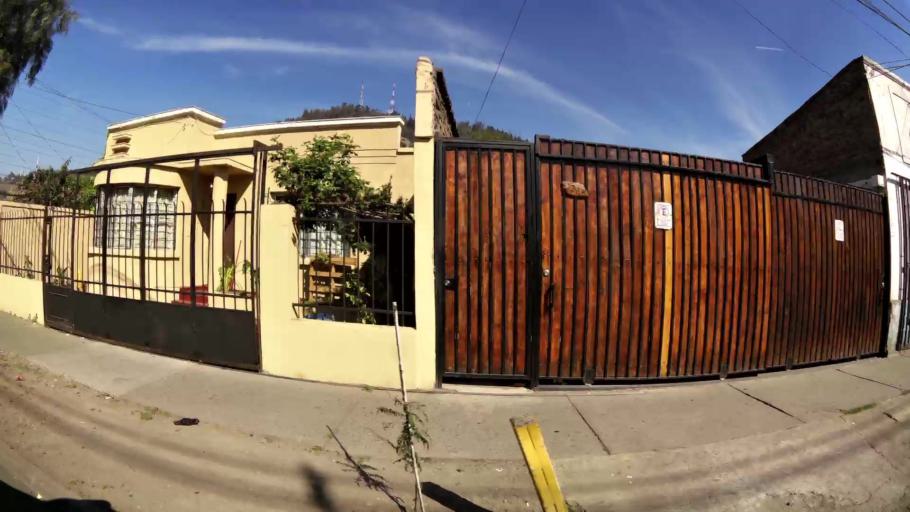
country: CL
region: Santiago Metropolitan
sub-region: Provincia de Santiago
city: Santiago
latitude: -33.4128
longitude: -70.6360
